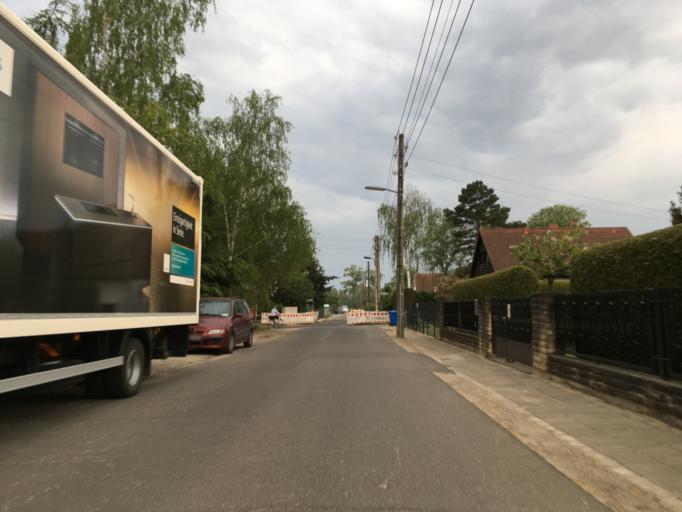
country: DE
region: Berlin
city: Wartenberg
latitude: 52.5833
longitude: 13.5287
